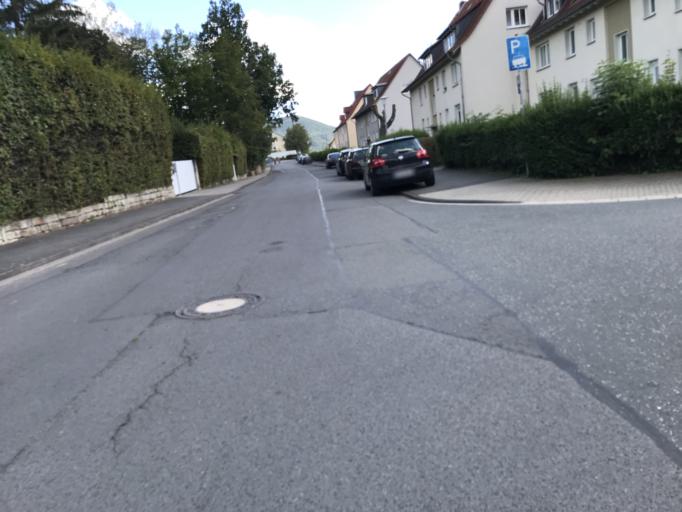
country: DE
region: Hesse
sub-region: Regierungsbezirk Kassel
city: Bad Sooden-Allendorf
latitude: 51.2697
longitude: 9.9815
